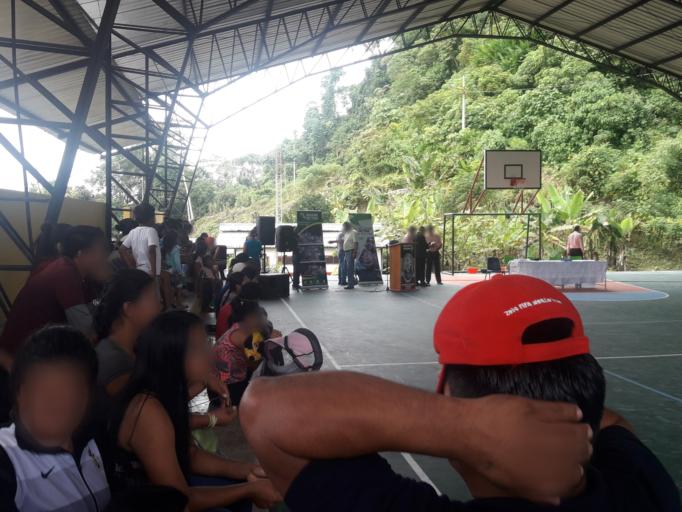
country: EC
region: Orellana
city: Boca Suno
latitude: -0.8769
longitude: -77.2624
